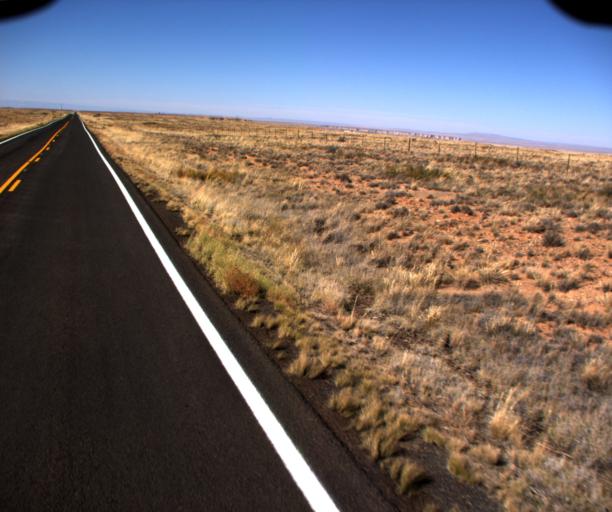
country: US
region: Arizona
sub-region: Coconino County
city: Tuba City
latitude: 35.9703
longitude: -110.9623
